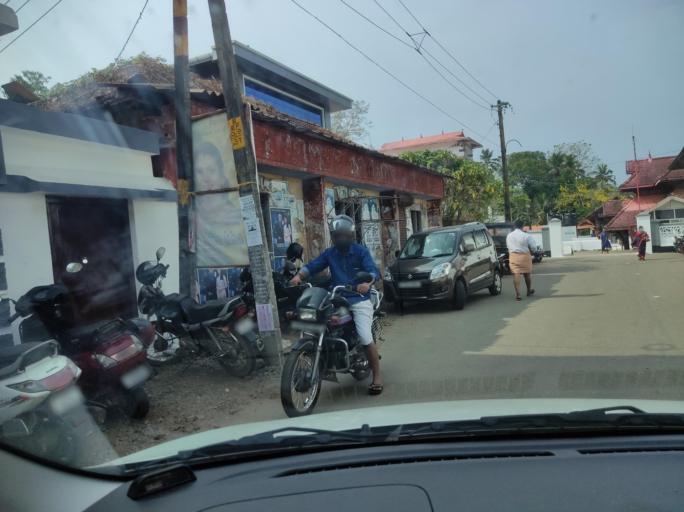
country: IN
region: Kerala
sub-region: Kottayam
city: Kottayam
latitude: 9.6730
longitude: 76.5606
